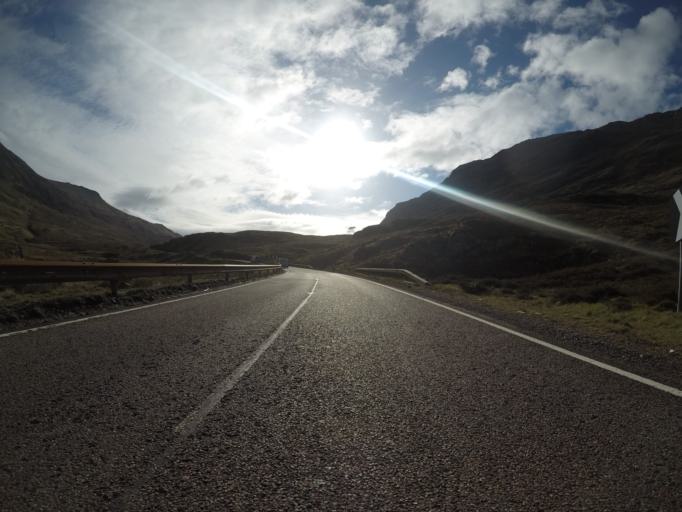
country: GB
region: Scotland
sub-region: Highland
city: Fort William
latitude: 56.6622
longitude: -4.9555
